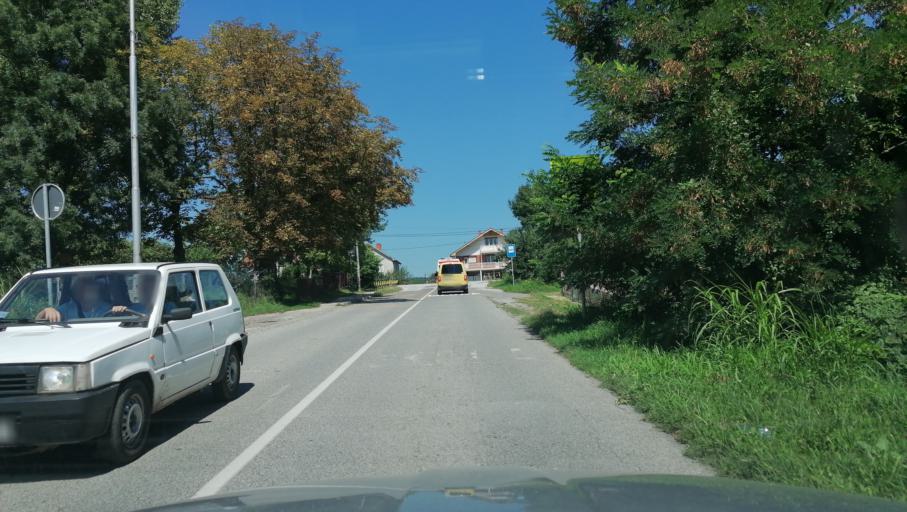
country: RS
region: Central Serbia
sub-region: Raski Okrug
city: Kraljevo
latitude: 43.6953
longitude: 20.5956
